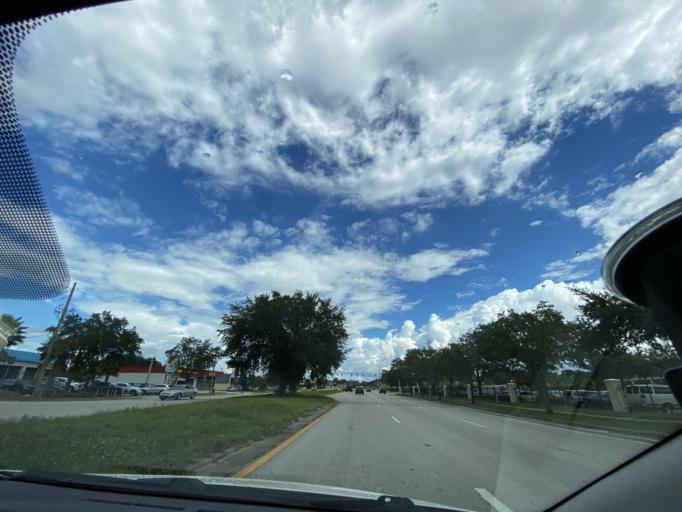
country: US
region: Florida
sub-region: Orange County
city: Orlando
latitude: 28.5528
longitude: -81.4121
